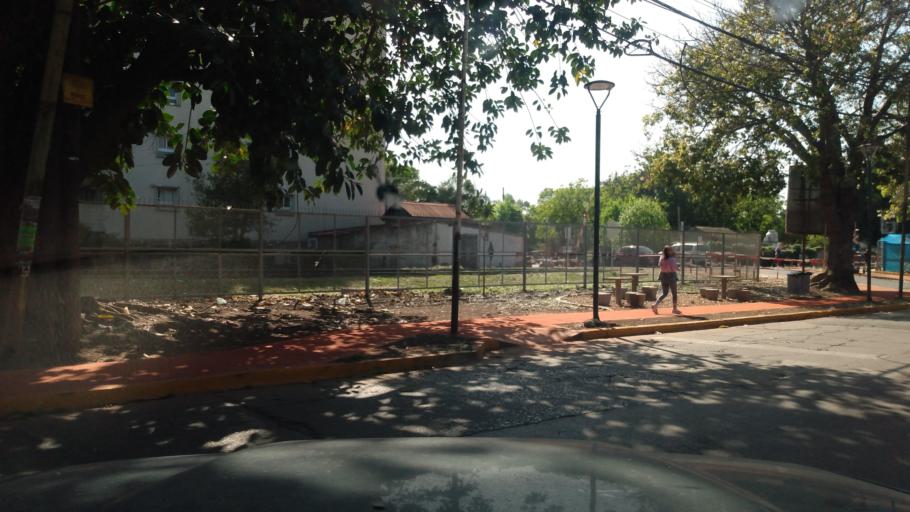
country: AR
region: Buenos Aires
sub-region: Partido de Moron
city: Moron
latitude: -34.6463
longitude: -58.5891
